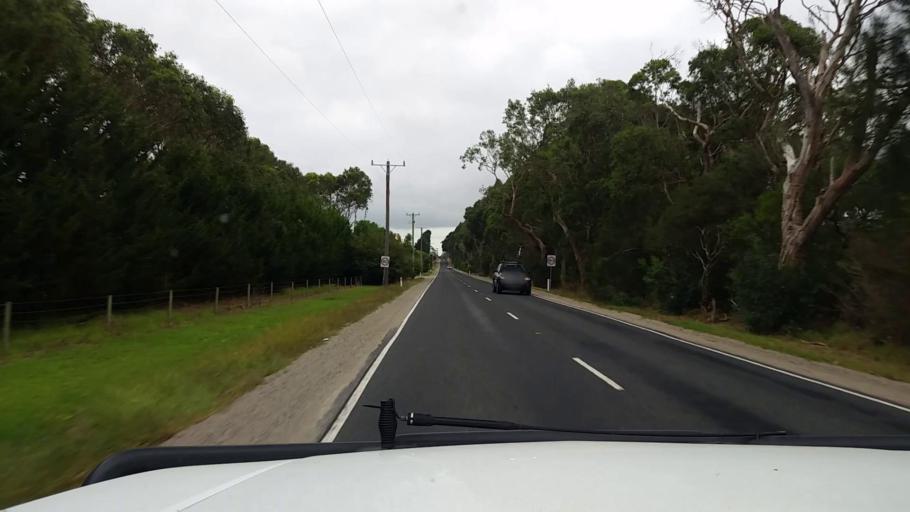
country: AU
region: Victoria
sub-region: Mornington Peninsula
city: Tyabb
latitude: -38.2680
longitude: 145.1456
